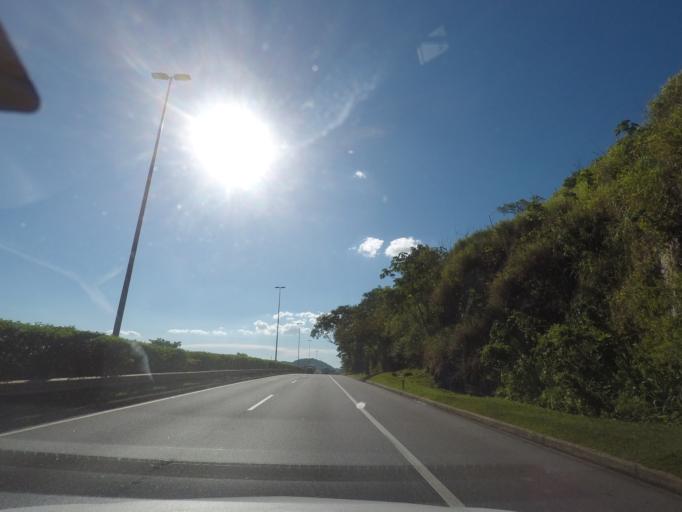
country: BR
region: Rio de Janeiro
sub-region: Sao Goncalo
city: Sao Goncalo
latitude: -22.6656
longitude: -43.1044
